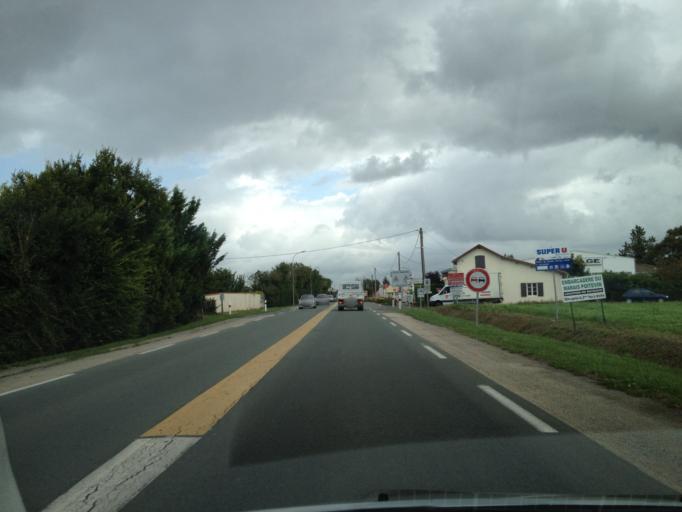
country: FR
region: Poitou-Charentes
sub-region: Departement de la Charente-Maritime
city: Marans
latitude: 46.2983
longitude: -0.9908
